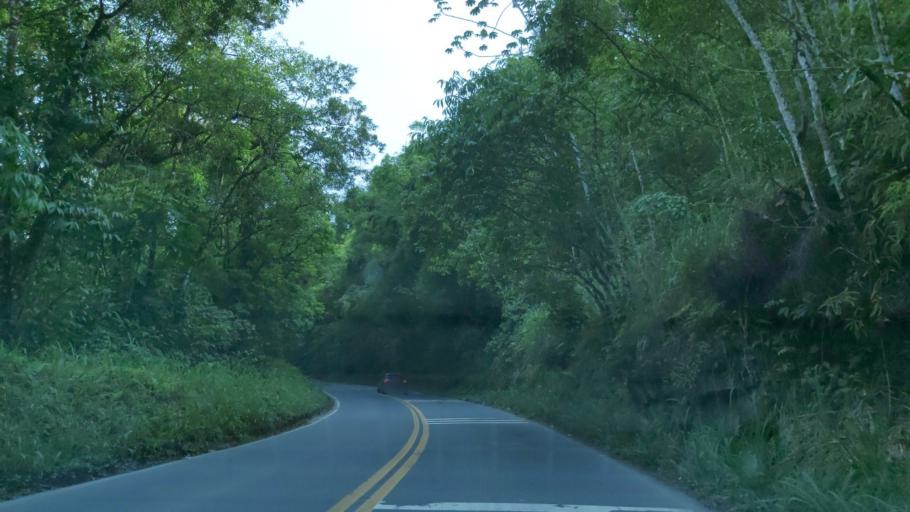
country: BR
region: Sao Paulo
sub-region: Juquia
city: Juquia
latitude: -24.1089
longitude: -47.6287
